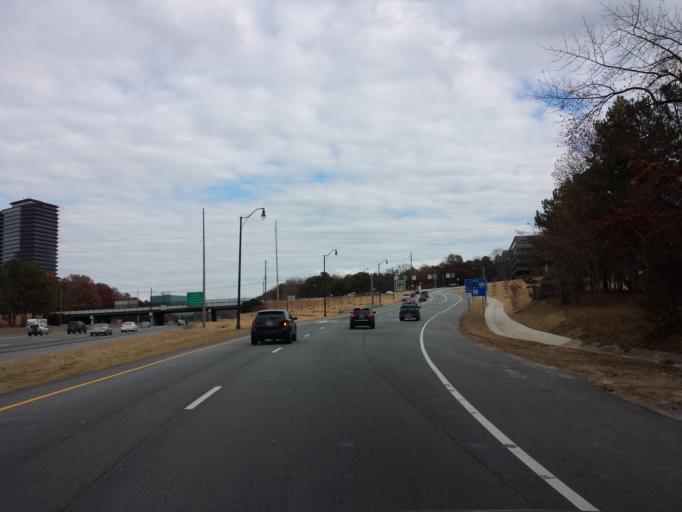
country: US
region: Georgia
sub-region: DeKalb County
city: Dunwoody
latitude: 33.9170
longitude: -84.3407
